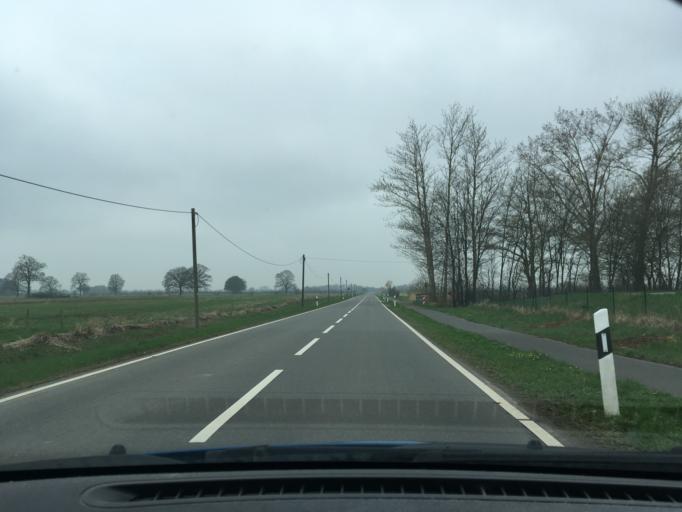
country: DE
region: Lower Saxony
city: Neu Darchau
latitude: 53.3124
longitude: 10.8879
